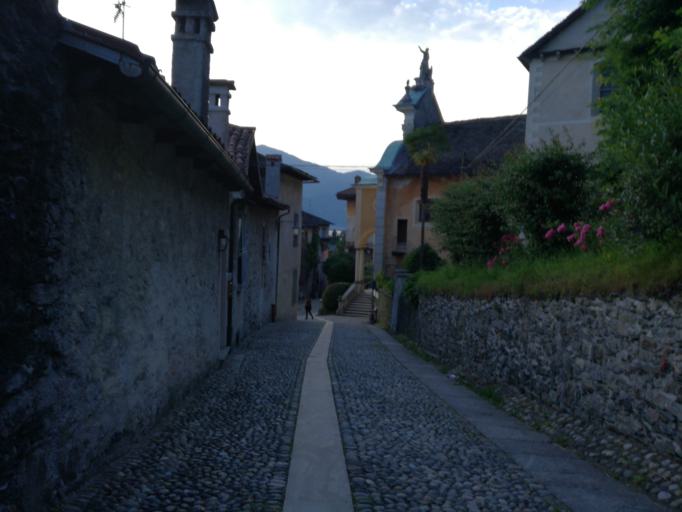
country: IT
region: Piedmont
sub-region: Provincia di Novara
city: Orta San Giulio
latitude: 45.7981
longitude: 8.4076
